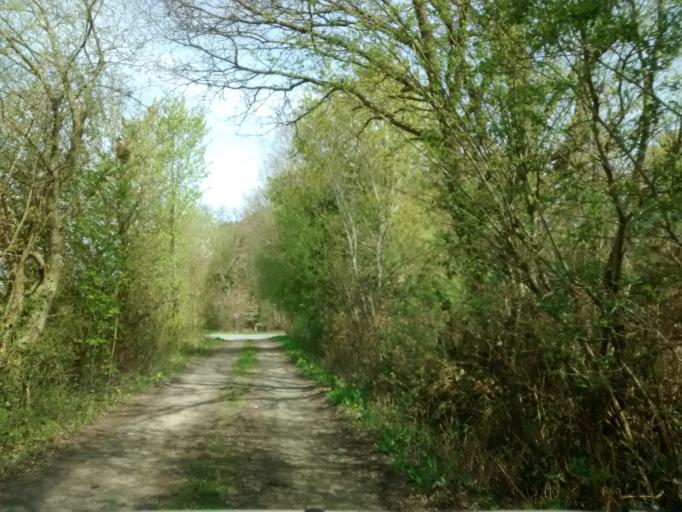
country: FR
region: Brittany
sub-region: Departement d'Ille-et-Vilaine
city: Fouillard
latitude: 48.1685
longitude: -1.5962
